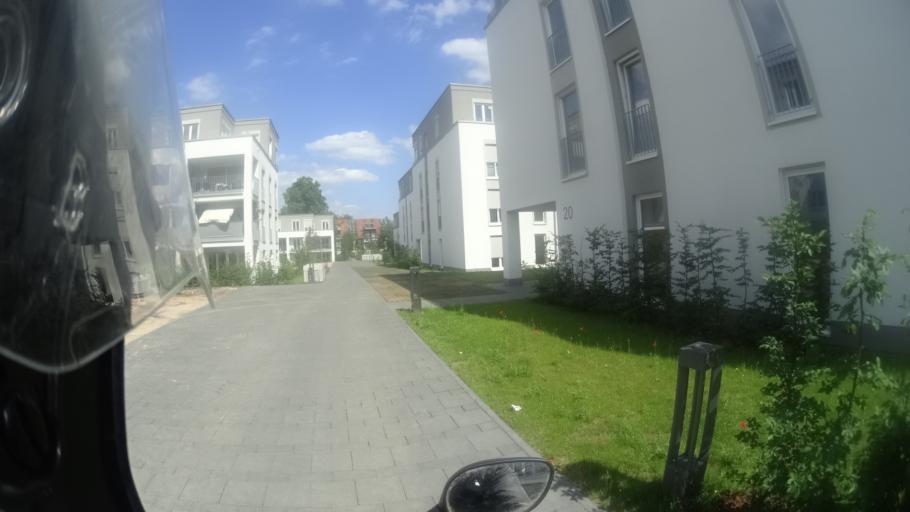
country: DE
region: Rheinland-Pfalz
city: Budenheim
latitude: 50.0439
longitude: 8.1915
